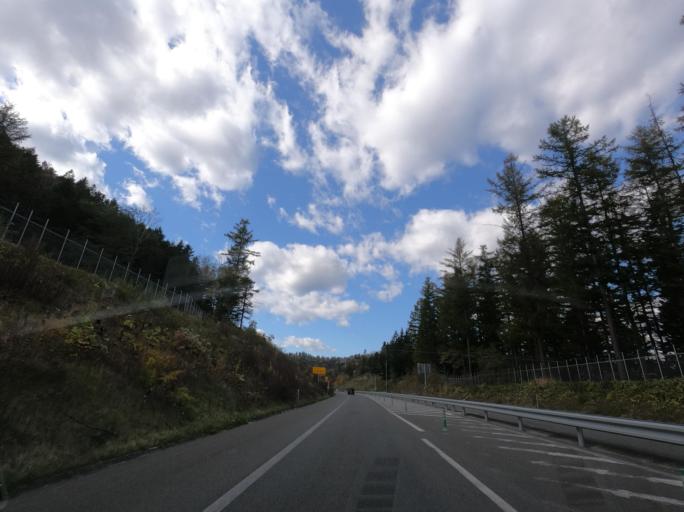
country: JP
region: Hokkaido
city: Kushiro
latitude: 43.0797
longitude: 144.0532
